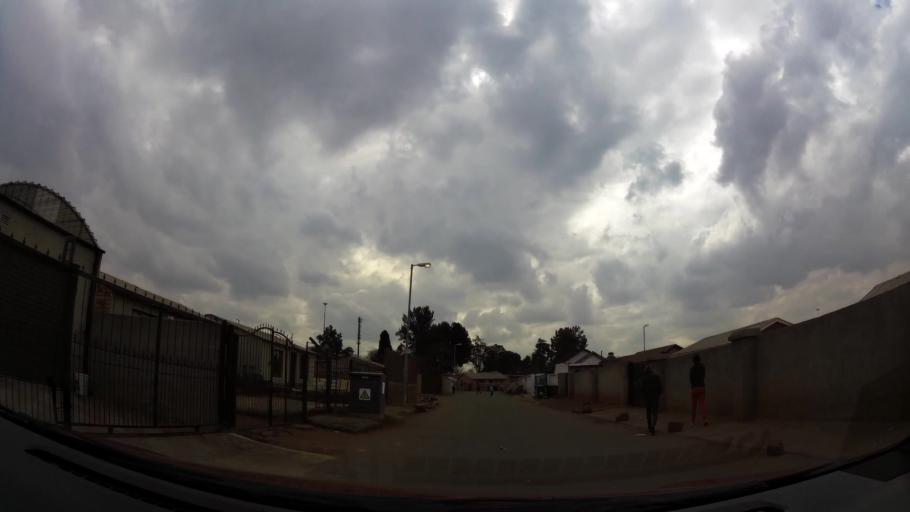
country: ZA
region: Gauteng
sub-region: City of Johannesburg Metropolitan Municipality
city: Soweto
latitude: -26.2637
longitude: 27.8356
